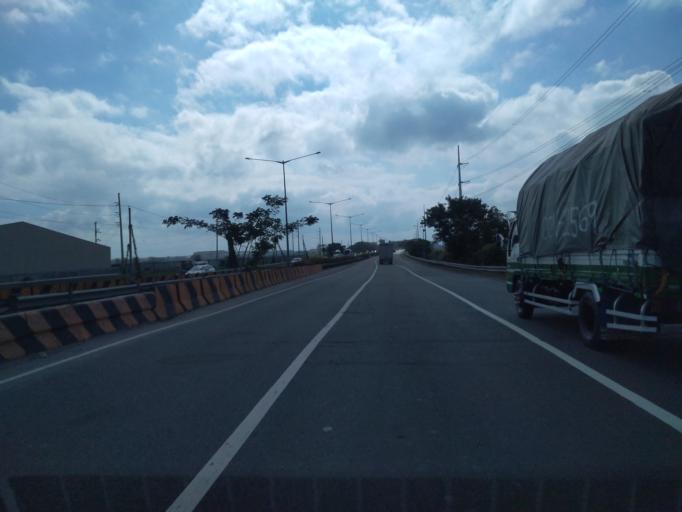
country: PH
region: Central Luzon
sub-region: Province of Pampanga
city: Pau
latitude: 15.0137
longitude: 120.7336
